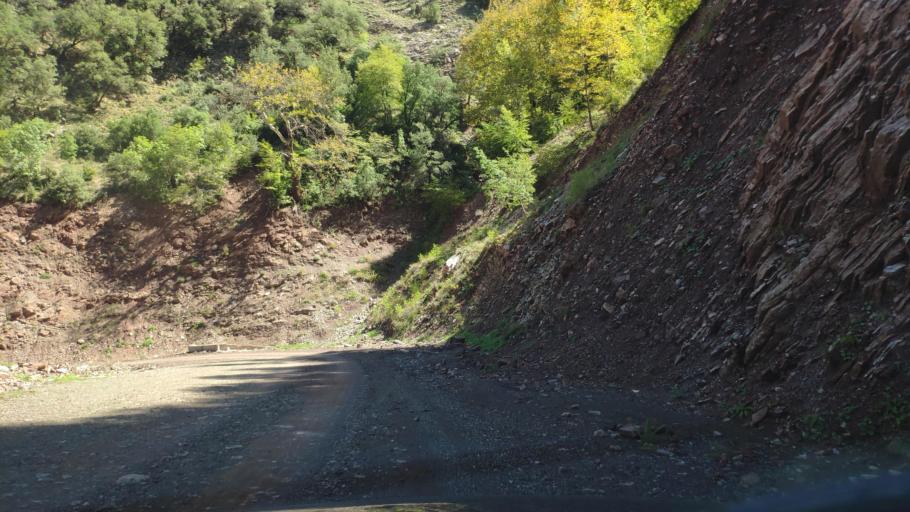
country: GR
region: Central Greece
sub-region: Nomos Evrytanias
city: Kerasochori
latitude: 39.1244
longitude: 21.6276
